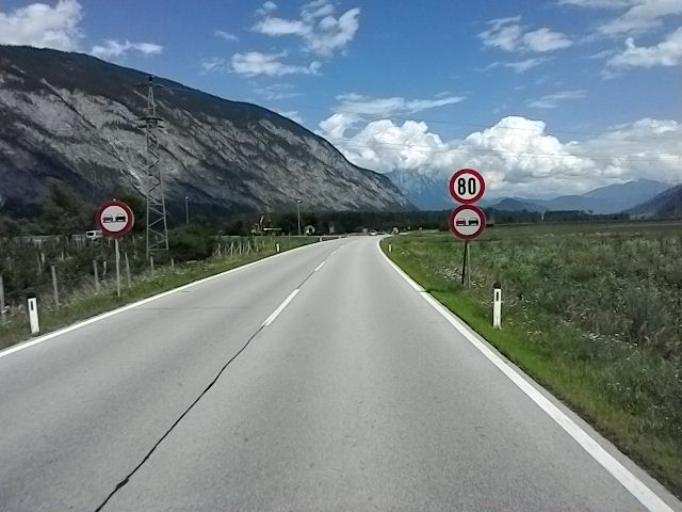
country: AT
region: Tyrol
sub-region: Politischer Bezirk Imst
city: Haiming
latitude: 47.2549
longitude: 10.8944
